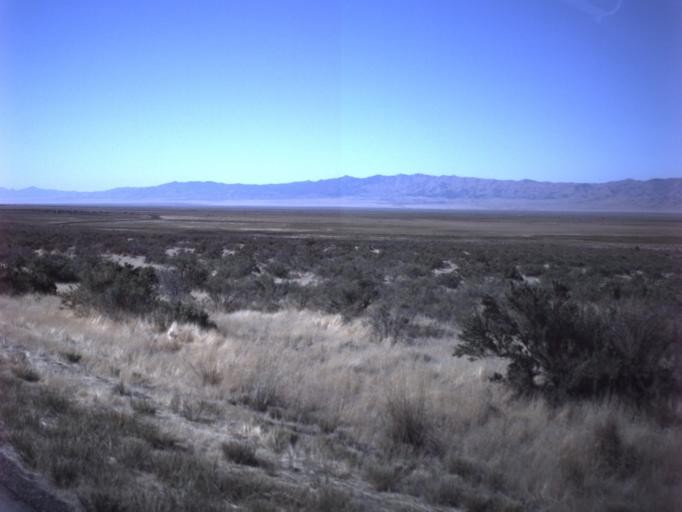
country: US
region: Utah
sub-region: Tooele County
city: Grantsville
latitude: 40.6424
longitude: -112.6888
